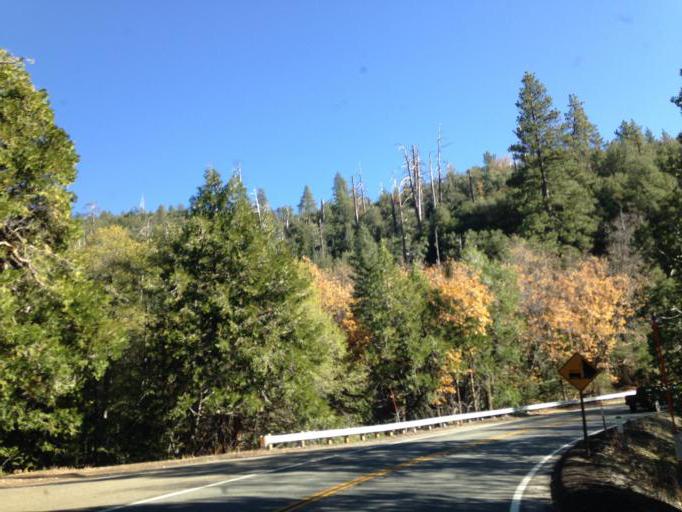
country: US
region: California
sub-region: Riverside County
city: Idyllwild-Pine Cove
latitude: 33.7970
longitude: -116.7414
